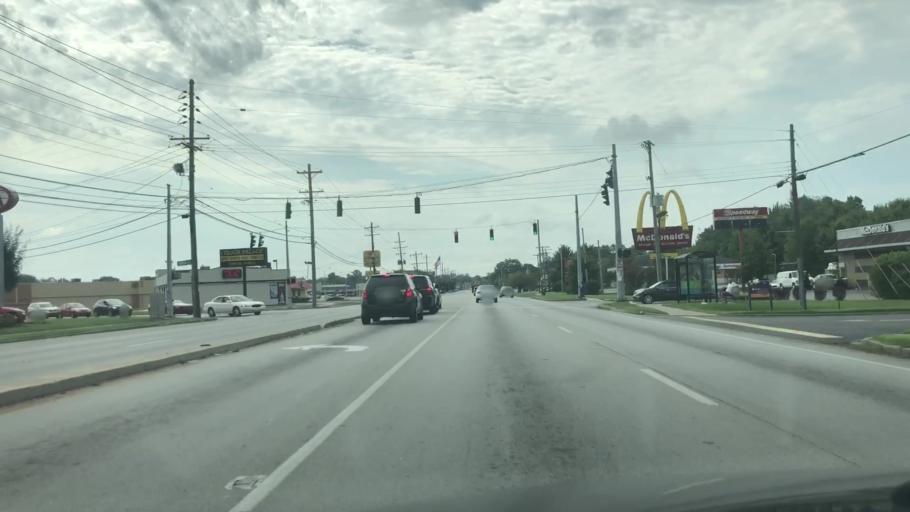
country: US
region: Kentucky
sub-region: Jefferson County
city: Okolona
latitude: 38.1691
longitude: -85.7070
